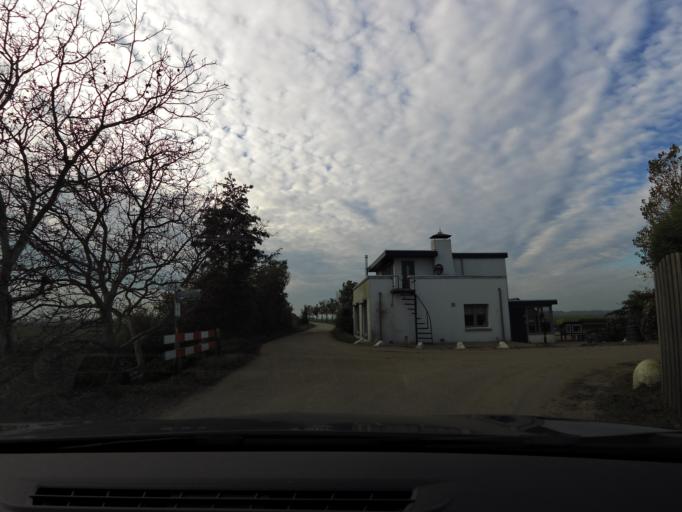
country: NL
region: South Holland
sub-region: Gemeente Goeree-Overflakkee
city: Middelharnis
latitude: 51.7178
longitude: 4.2080
